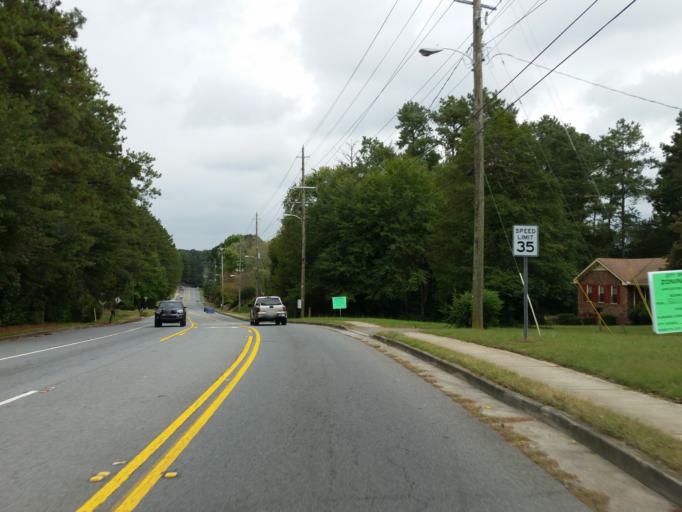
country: US
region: Georgia
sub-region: Cobb County
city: Smyrna
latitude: 33.9333
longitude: -84.4807
